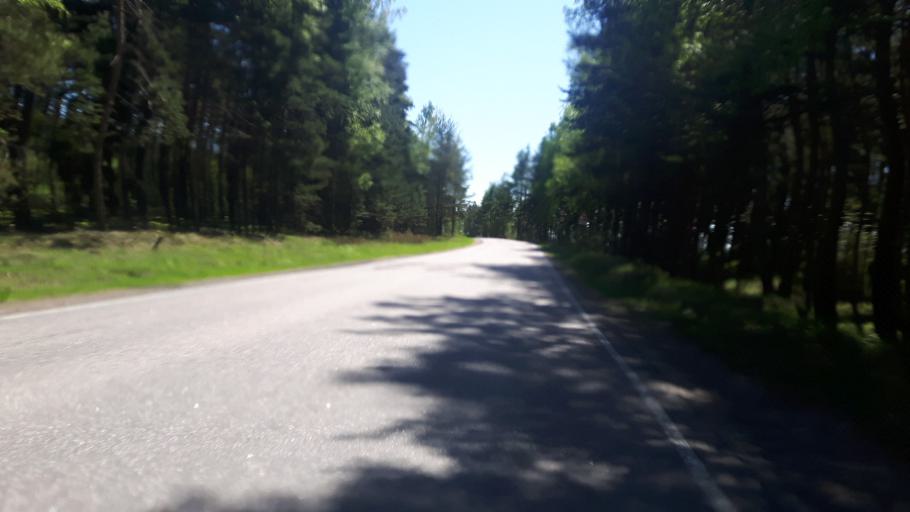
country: RU
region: Leningrad
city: Glebychevo
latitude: 60.3283
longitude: 28.8233
